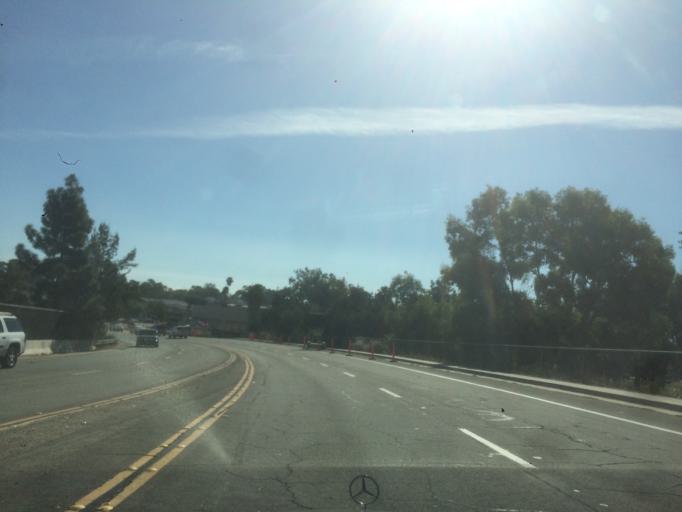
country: US
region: California
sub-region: Santa Barbara County
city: Goleta
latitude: 34.4383
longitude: -119.8323
